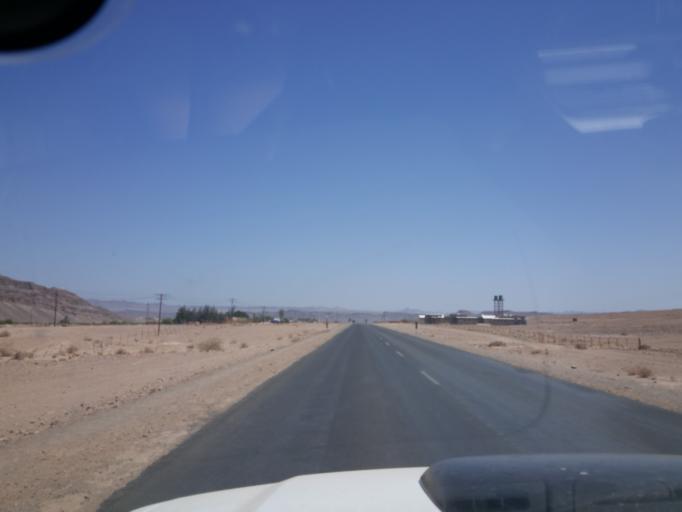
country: ZA
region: Northern Cape
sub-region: Namakwa District Municipality
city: Port Nolloth
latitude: -28.7495
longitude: 17.6189
